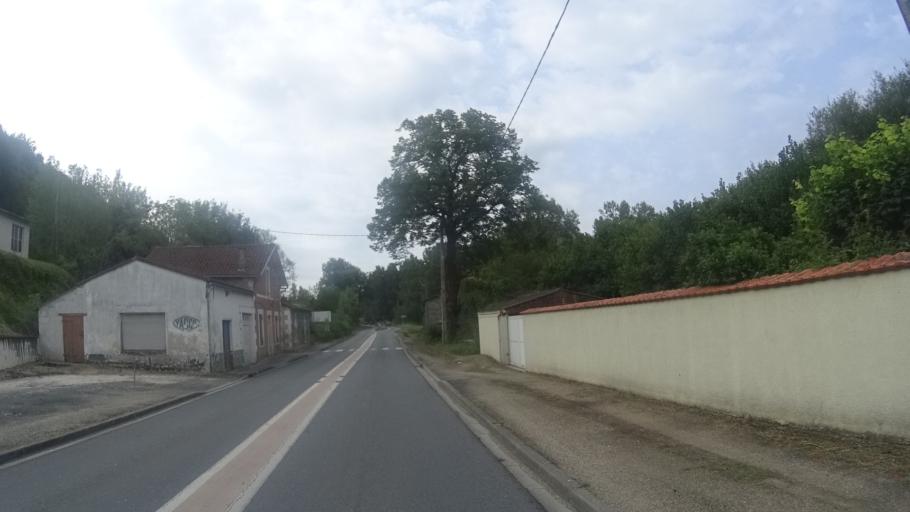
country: FR
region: Aquitaine
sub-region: Departement de la Dordogne
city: Riberac
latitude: 45.2284
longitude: 0.3576
